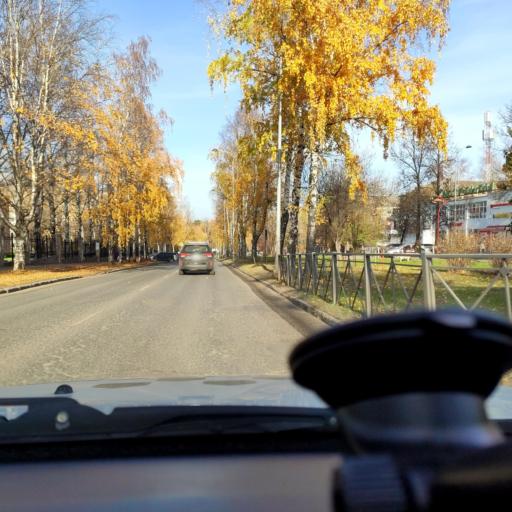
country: RU
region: Perm
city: Perm
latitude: 57.9794
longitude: 56.1831
